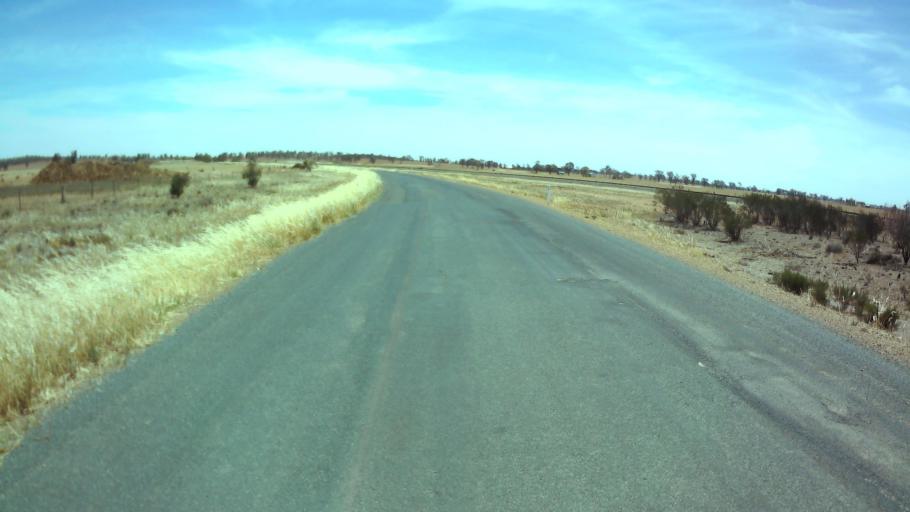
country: AU
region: New South Wales
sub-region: Weddin
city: Grenfell
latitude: -33.7541
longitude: 147.7643
